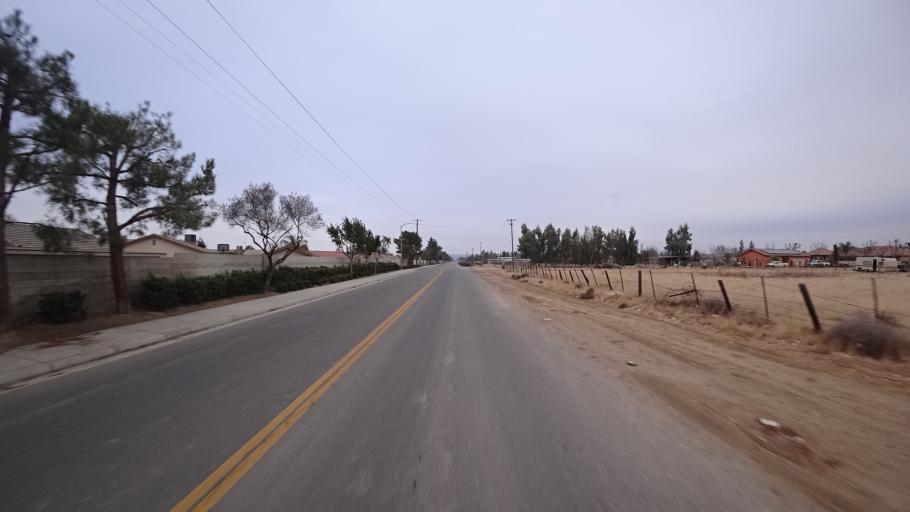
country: US
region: California
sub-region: Kern County
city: Bakersfield
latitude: 35.3428
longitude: -118.9409
